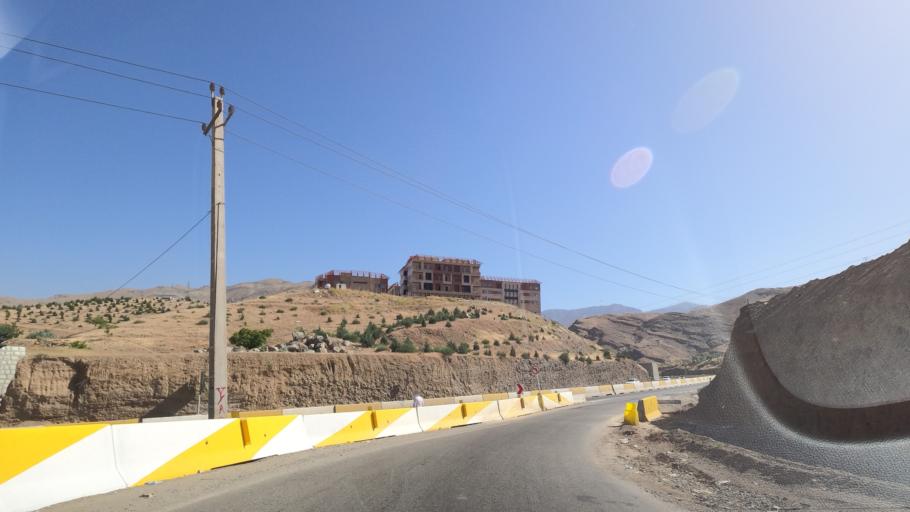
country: IR
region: Alborz
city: Karaj
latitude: 35.8235
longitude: 51.0389
